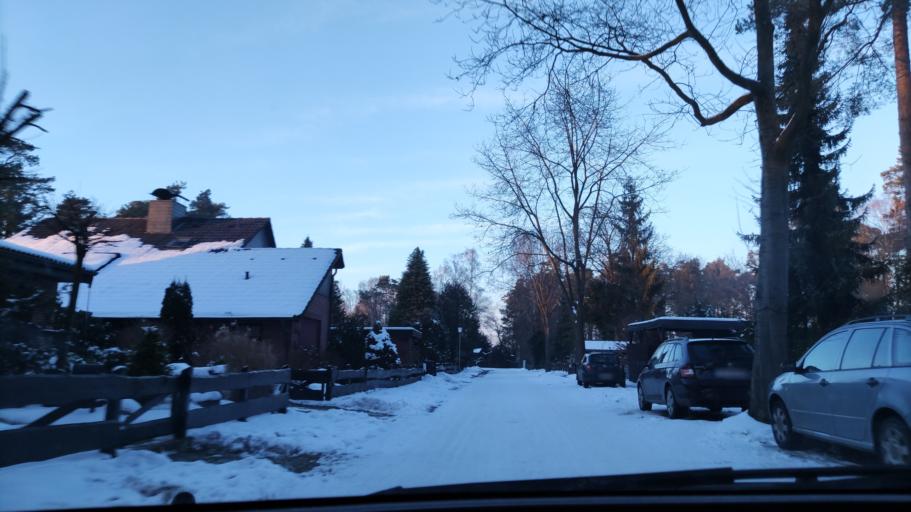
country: DE
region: Lower Saxony
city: Bleckede
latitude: 53.2936
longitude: 10.6907
